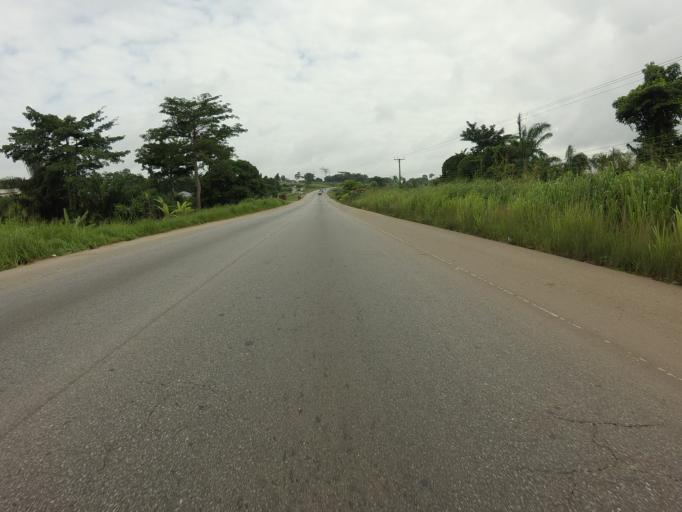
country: GH
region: Ashanti
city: Tafo
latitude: 6.9715
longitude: -1.6840
